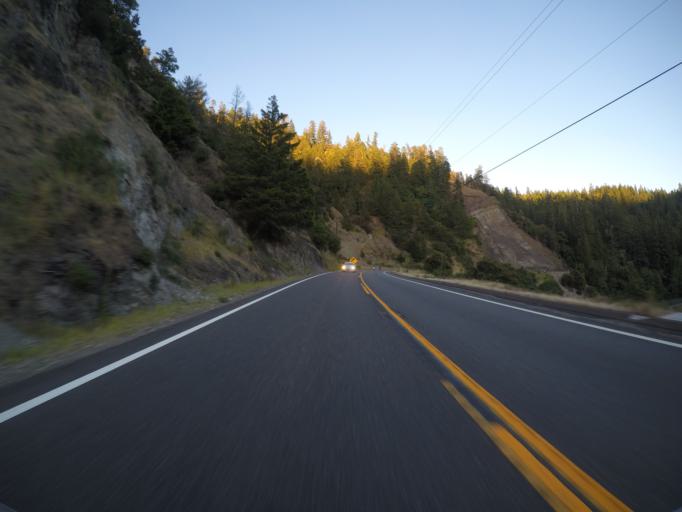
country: US
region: California
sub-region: Humboldt County
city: Redway
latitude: 39.9068
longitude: -123.7513
